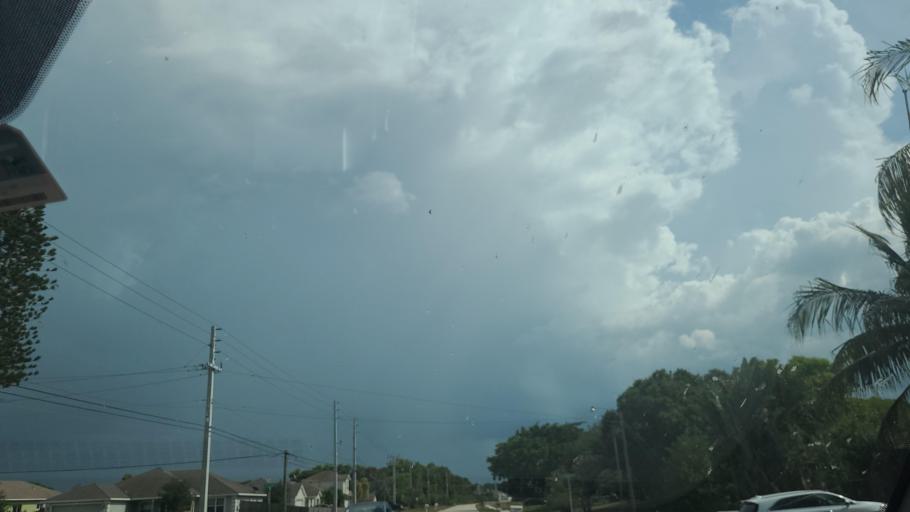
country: US
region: Florida
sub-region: Saint Lucie County
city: Port Saint Lucie
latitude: 27.2502
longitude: -80.3544
